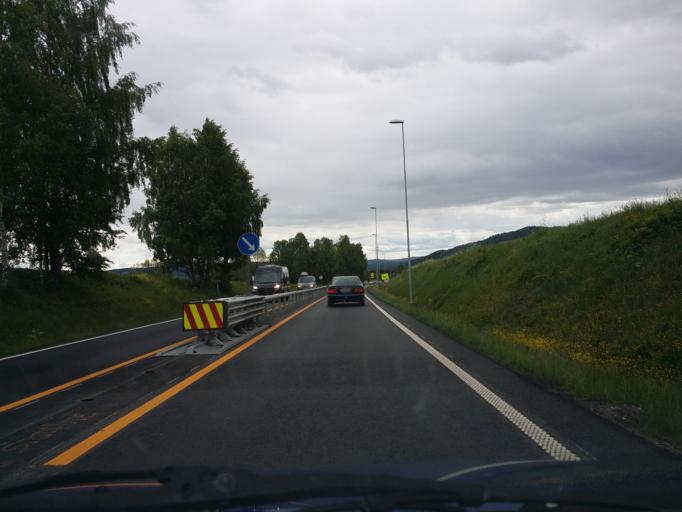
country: NO
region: Hedmark
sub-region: Ringsaker
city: Moelv
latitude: 60.9742
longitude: 10.5904
